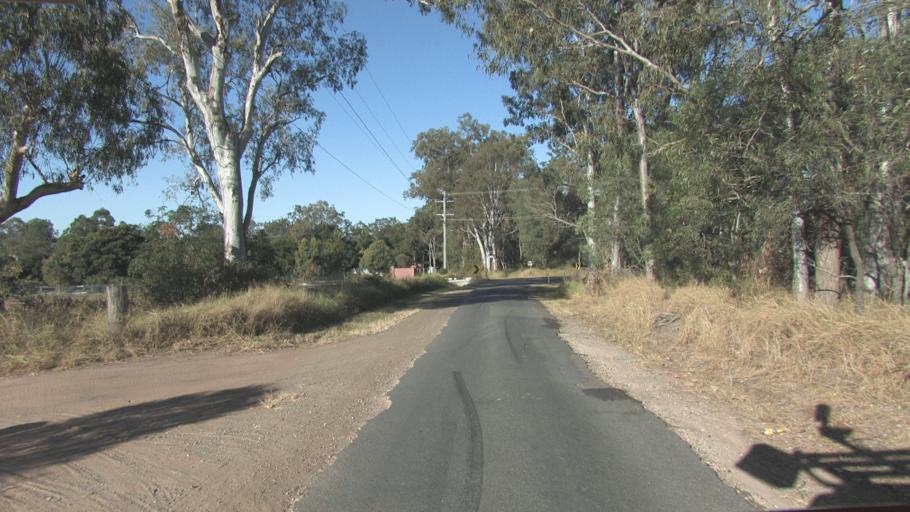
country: AU
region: Queensland
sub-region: Logan
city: North Maclean
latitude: -27.7786
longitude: 153.0396
